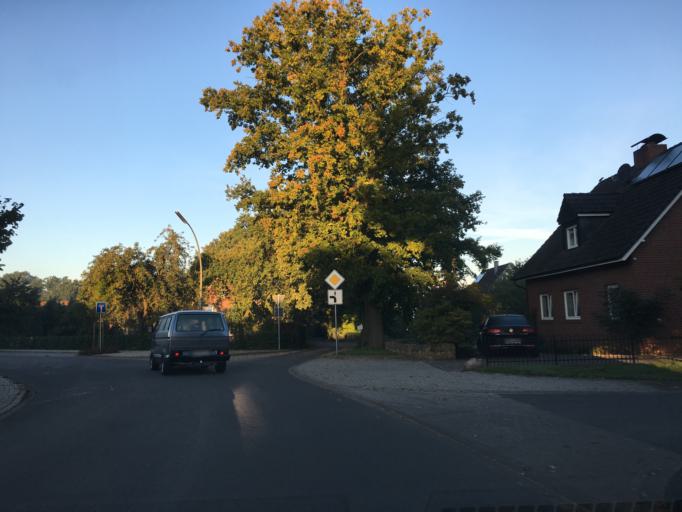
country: DE
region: North Rhine-Westphalia
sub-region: Regierungsbezirk Munster
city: Steinfurt
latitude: 52.1439
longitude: 7.3203
